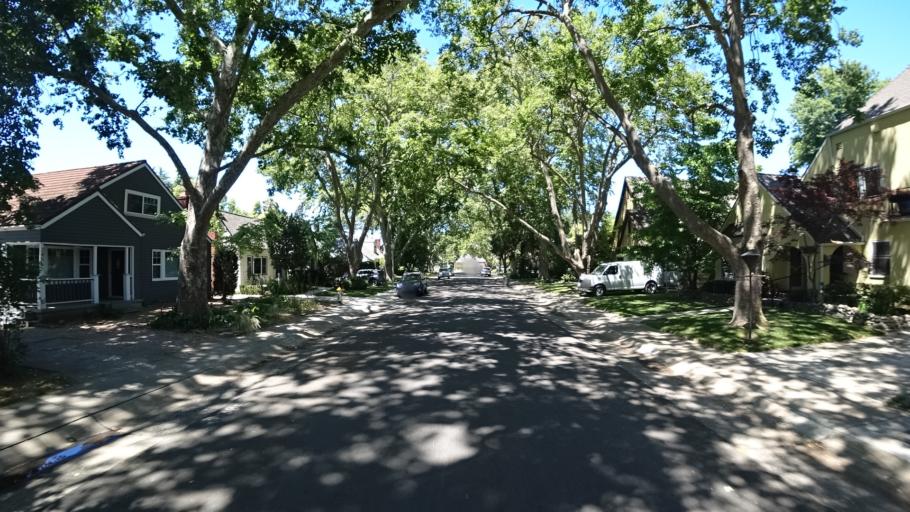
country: US
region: California
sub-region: Sacramento County
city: Sacramento
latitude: 38.5474
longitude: -121.4815
